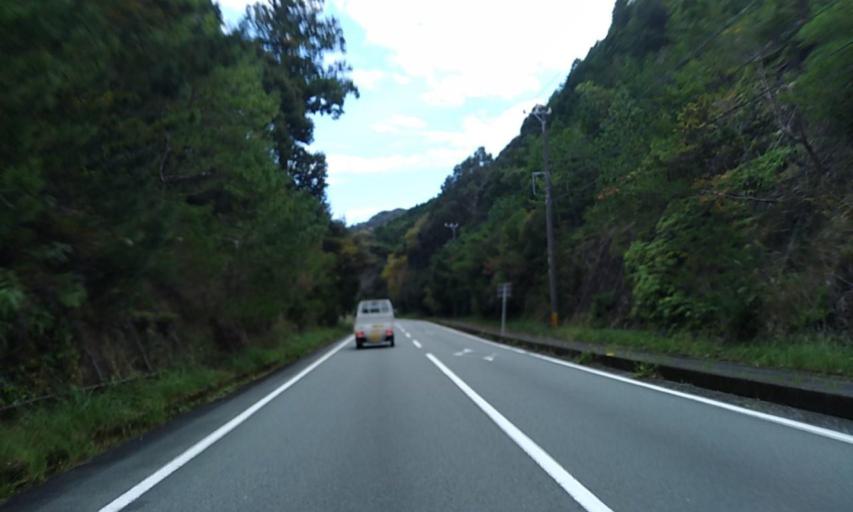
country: JP
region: Mie
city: Ise
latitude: 34.3004
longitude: 136.6075
